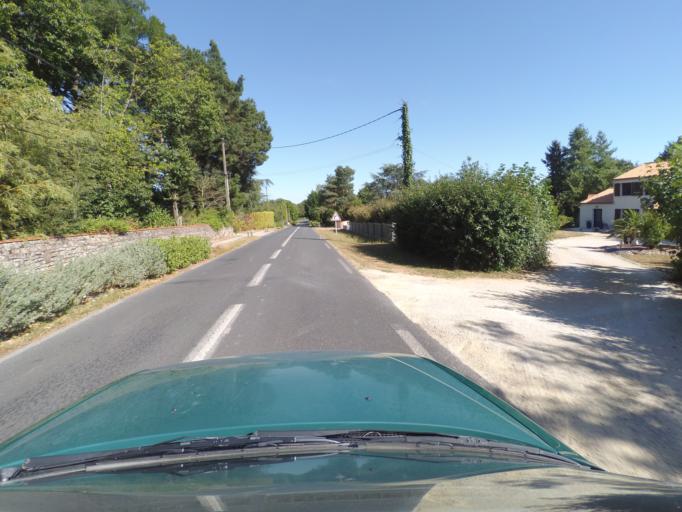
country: FR
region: Pays de la Loire
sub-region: Departement de la Loire-Atlantique
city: Maisdon-sur-Sevre
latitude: 47.0932
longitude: -1.3732
